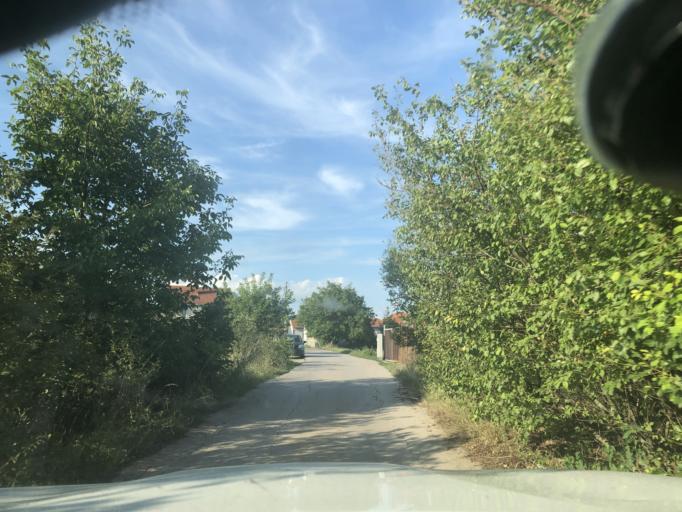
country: RS
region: Central Serbia
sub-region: Nisavski Okrug
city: Nis
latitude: 43.3261
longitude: 21.9549
